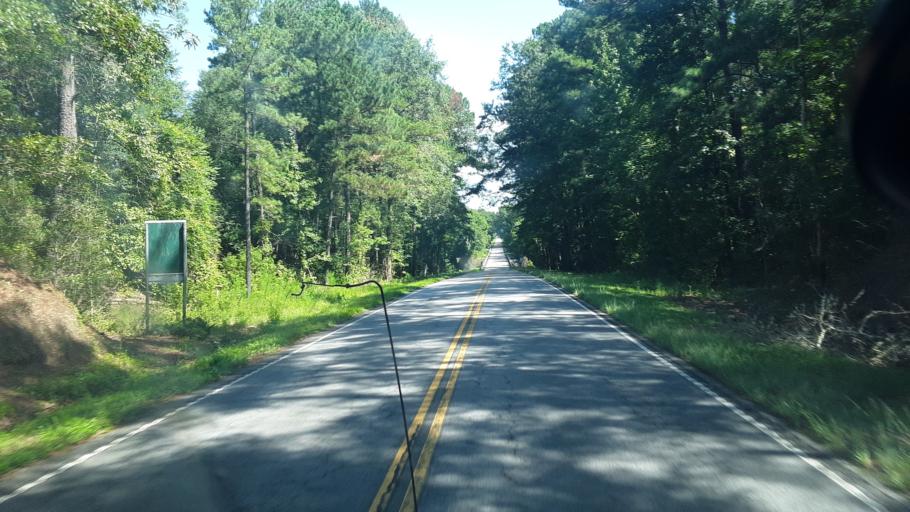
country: US
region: South Carolina
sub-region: Hampton County
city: Hampton
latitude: 32.9873
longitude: -81.0541
